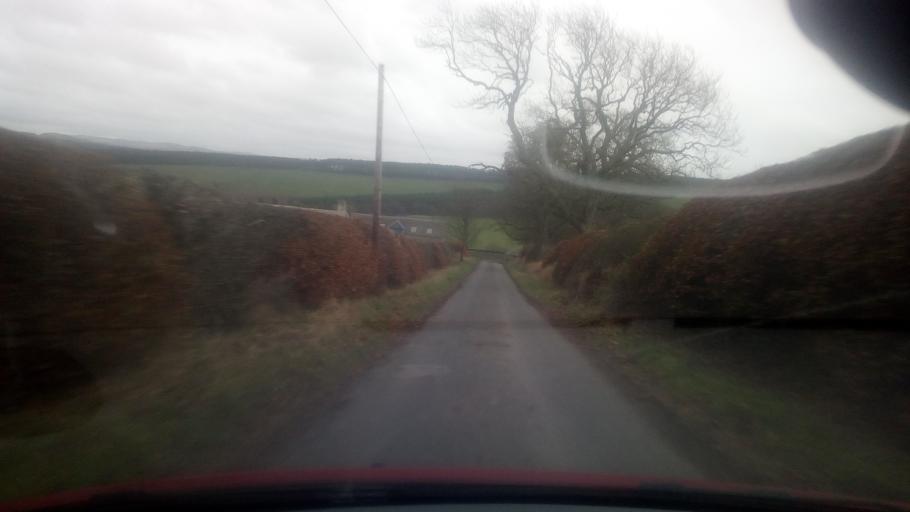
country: GB
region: Scotland
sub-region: The Scottish Borders
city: Jedburgh
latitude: 55.4604
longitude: -2.5141
